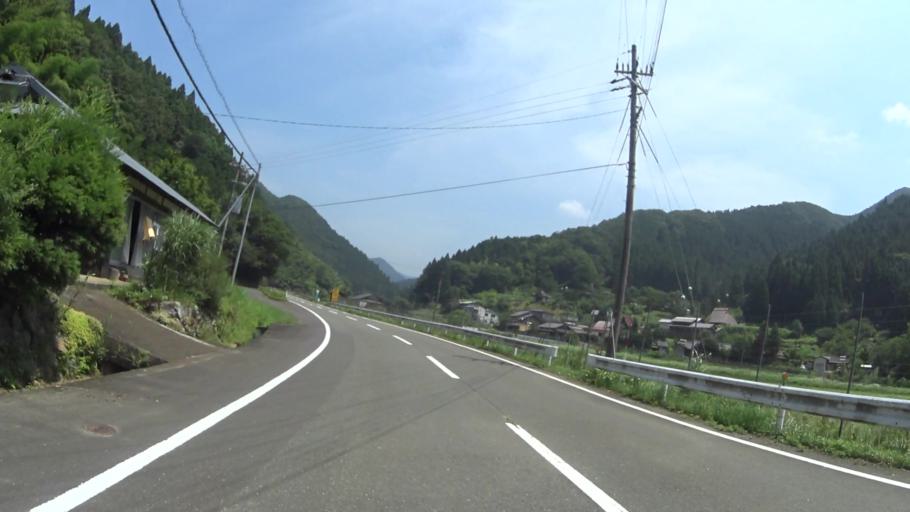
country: JP
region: Kyoto
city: Maizuru
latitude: 35.3037
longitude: 135.4269
